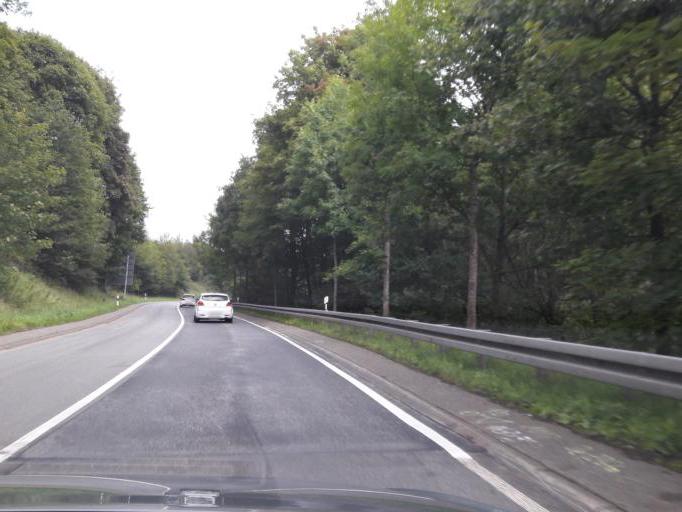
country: DE
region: Saarland
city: Freisen
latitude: 49.5551
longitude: 7.2626
